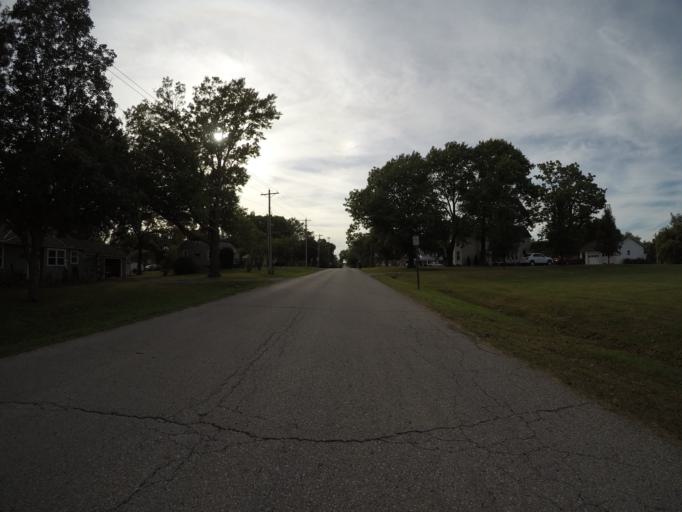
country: US
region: Kansas
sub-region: Douglas County
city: Baldwin City
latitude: 38.7750
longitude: -95.1807
